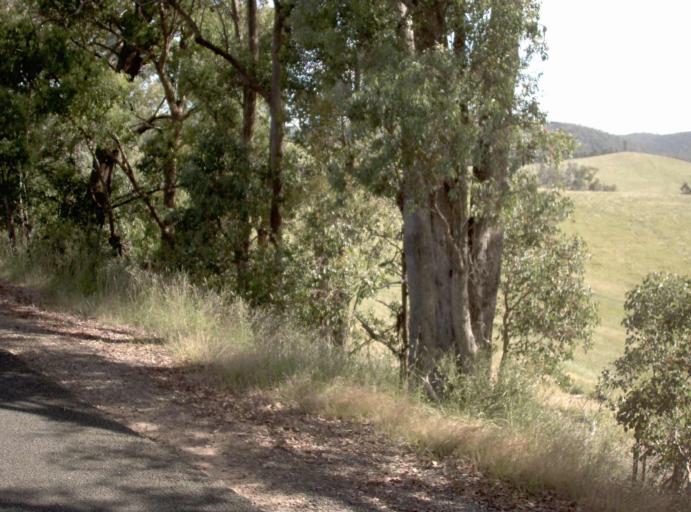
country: AU
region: Victoria
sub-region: East Gippsland
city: Lakes Entrance
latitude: -37.4928
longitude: 148.1312
